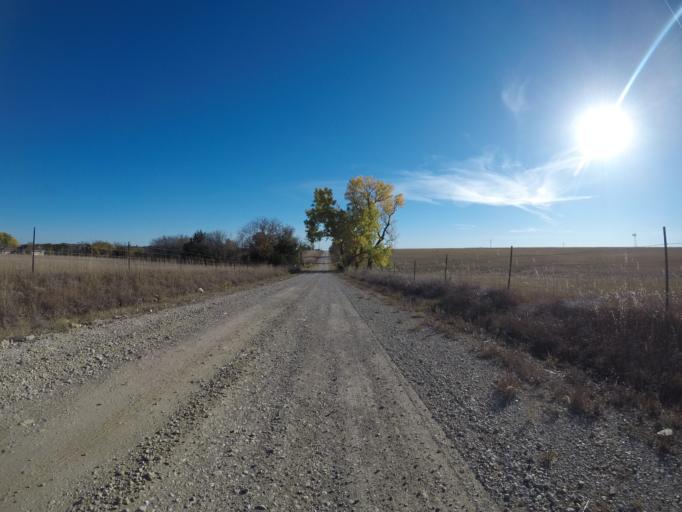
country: US
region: Kansas
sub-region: Riley County
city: Ogden
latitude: 39.2637
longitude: -96.7099
